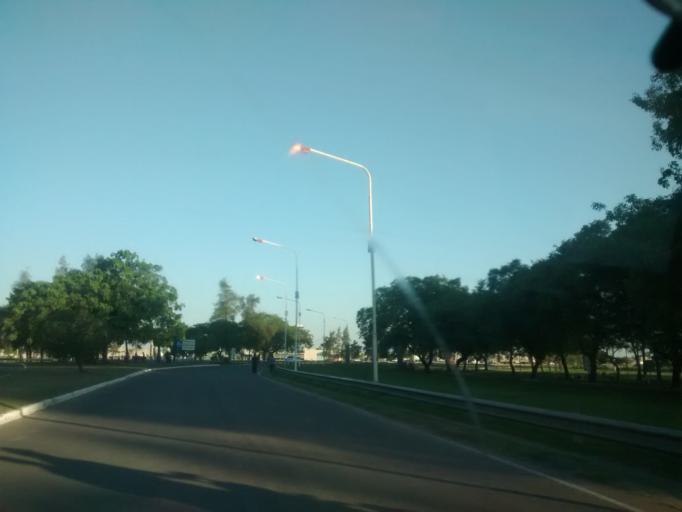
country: AR
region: Chaco
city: Fontana
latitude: -27.4439
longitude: -59.0254
